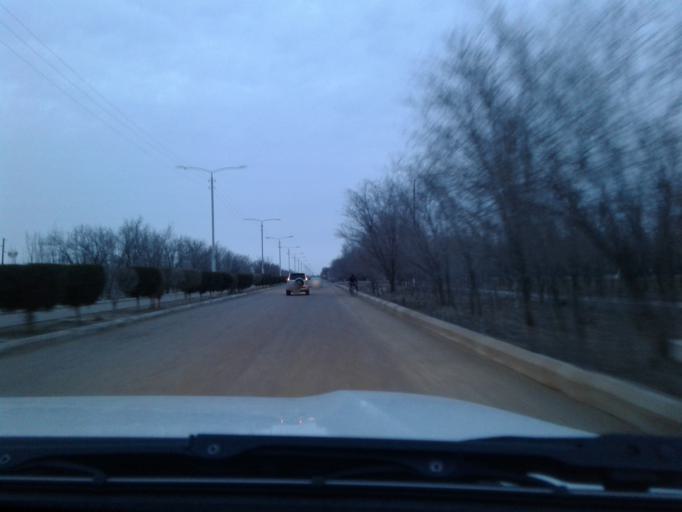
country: UZ
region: Karakalpakstan
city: Manghit
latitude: 42.0657
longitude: 59.9417
